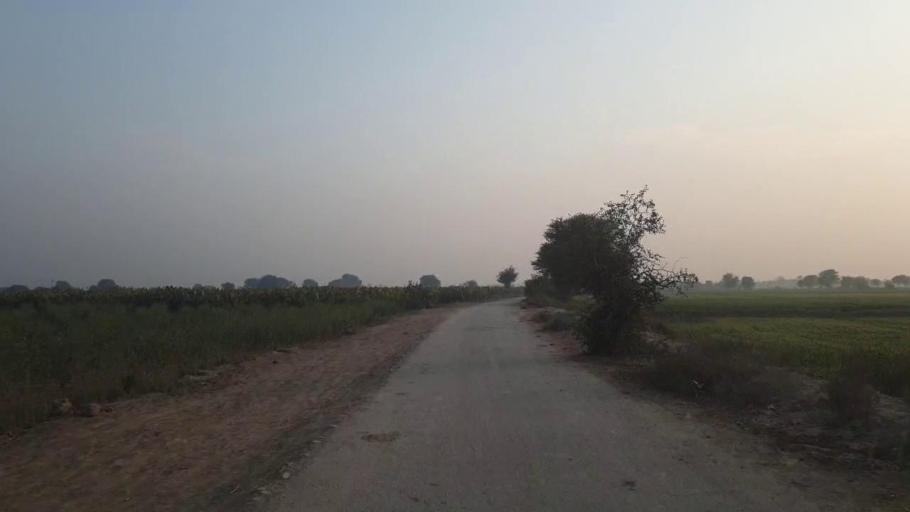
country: PK
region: Sindh
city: Bhit Shah
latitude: 25.7751
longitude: 68.4621
